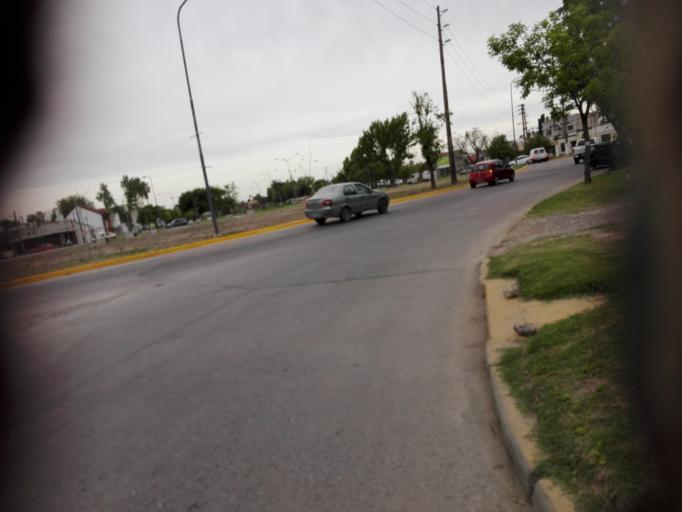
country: AR
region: Buenos Aires
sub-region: Partido de La Plata
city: La Plata
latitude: -34.9226
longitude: -57.9942
